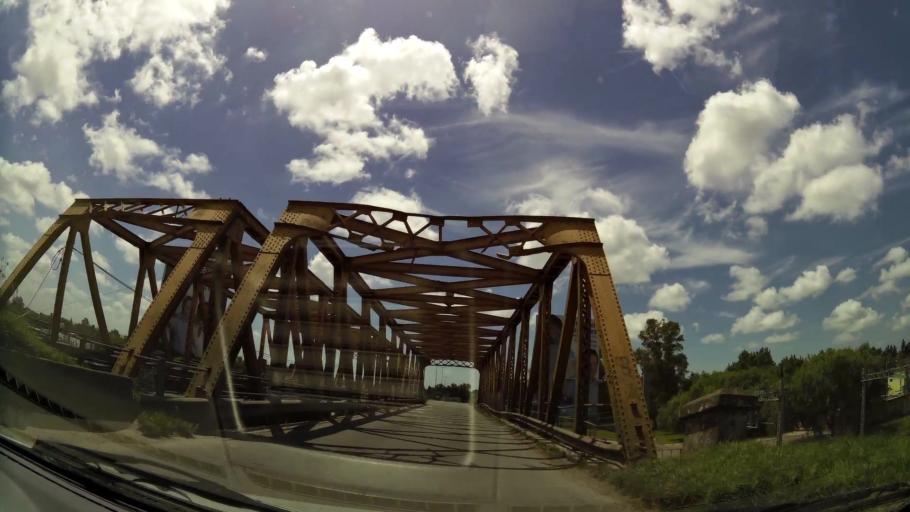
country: AR
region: Buenos Aires
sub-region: Partido de Quilmes
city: Quilmes
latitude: -34.8210
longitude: -58.2263
